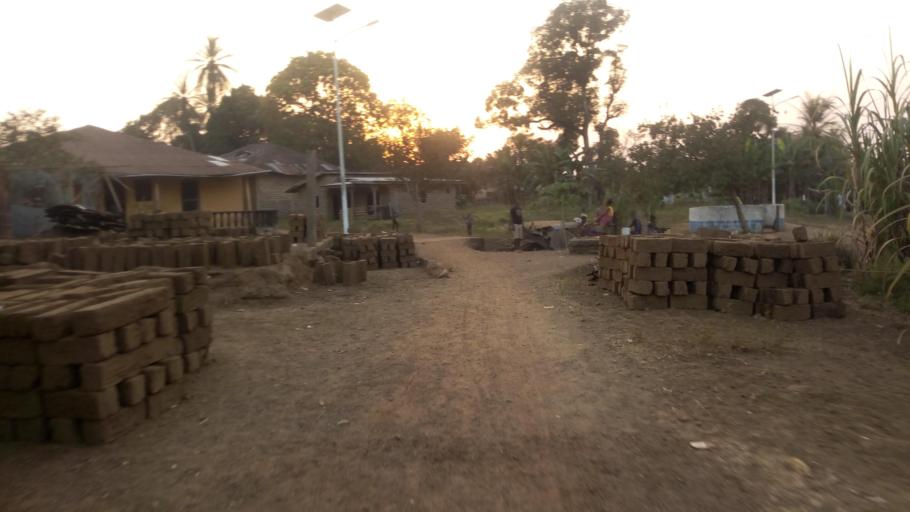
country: SL
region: Southern Province
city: Mogbwemo
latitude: 7.6075
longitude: -12.1789
